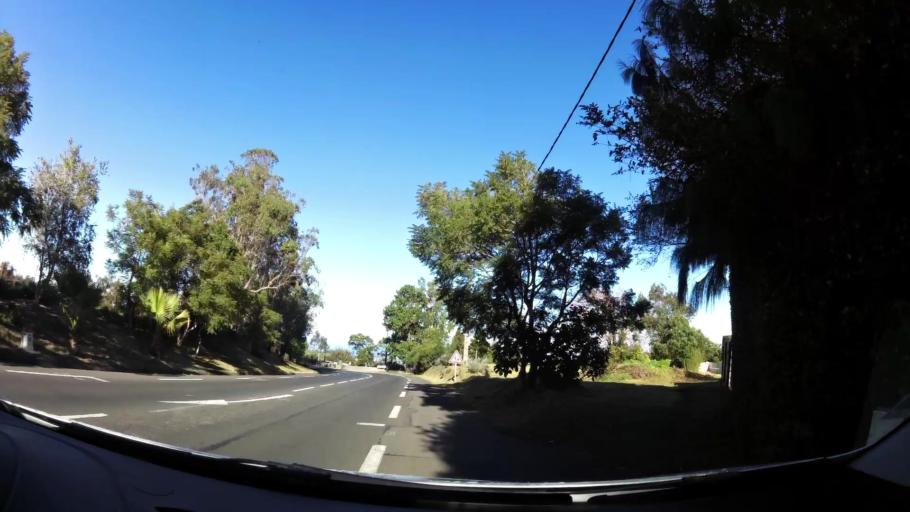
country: RE
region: Reunion
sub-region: Reunion
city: Le Tampon
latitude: -21.2068
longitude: 55.5680
